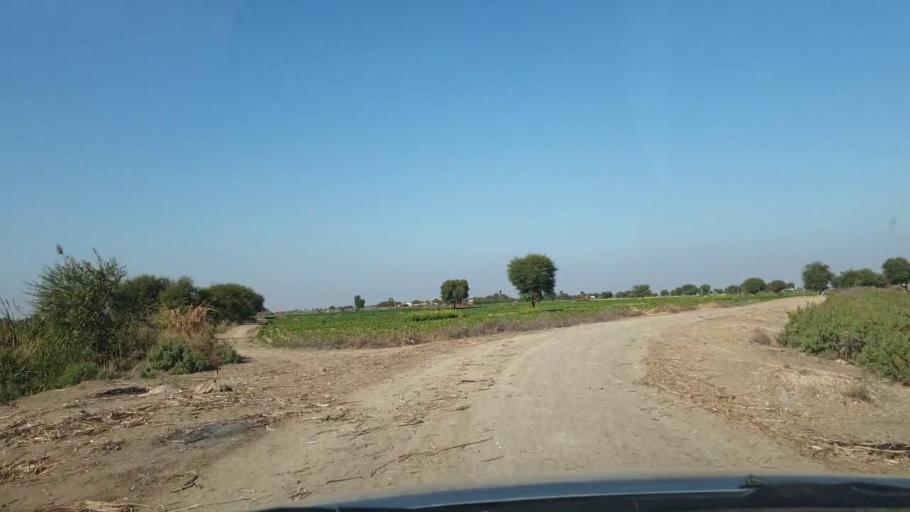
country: PK
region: Sindh
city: Jhol
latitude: 25.9204
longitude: 68.9867
